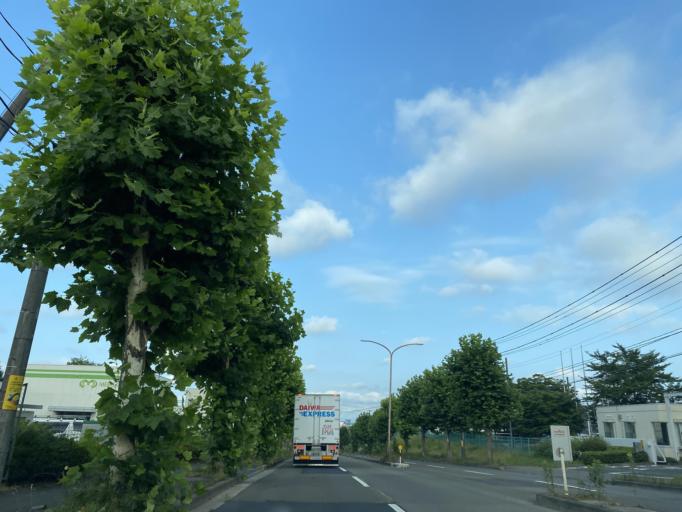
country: JP
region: Miyagi
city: Tomiya
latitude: 38.3553
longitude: 140.8565
